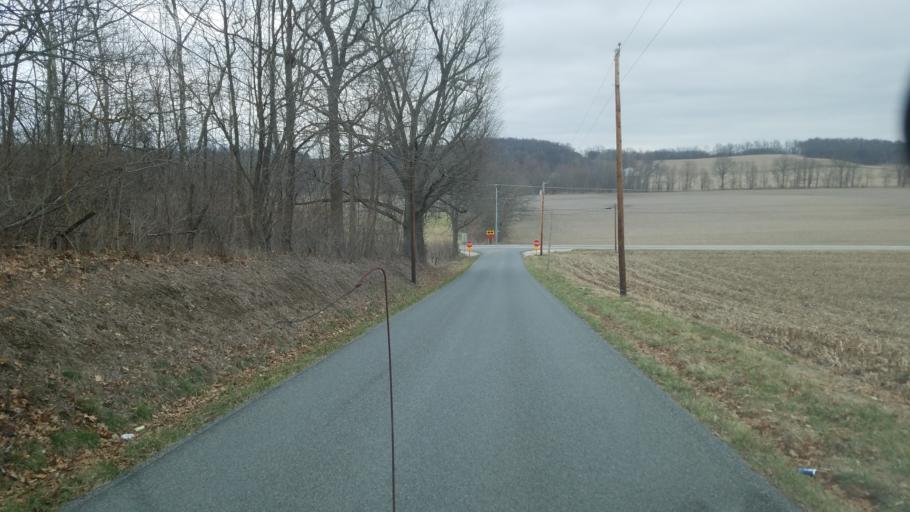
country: US
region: Ohio
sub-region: Licking County
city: Utica
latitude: 40.1983
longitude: -82.4025
